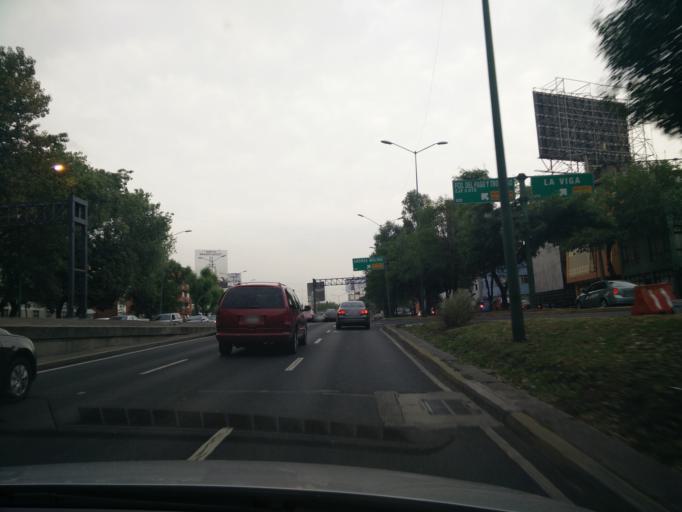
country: MX
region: Mexico City
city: Colonia Nativitas
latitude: 19.4031
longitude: -99.1328
